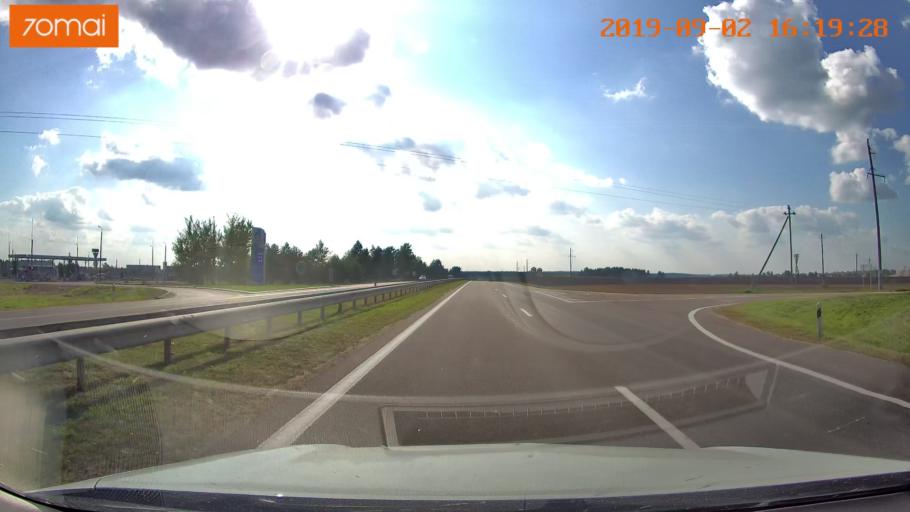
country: BY
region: Minsk
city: Chervyen'
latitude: 53.7261
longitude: 28.4089
